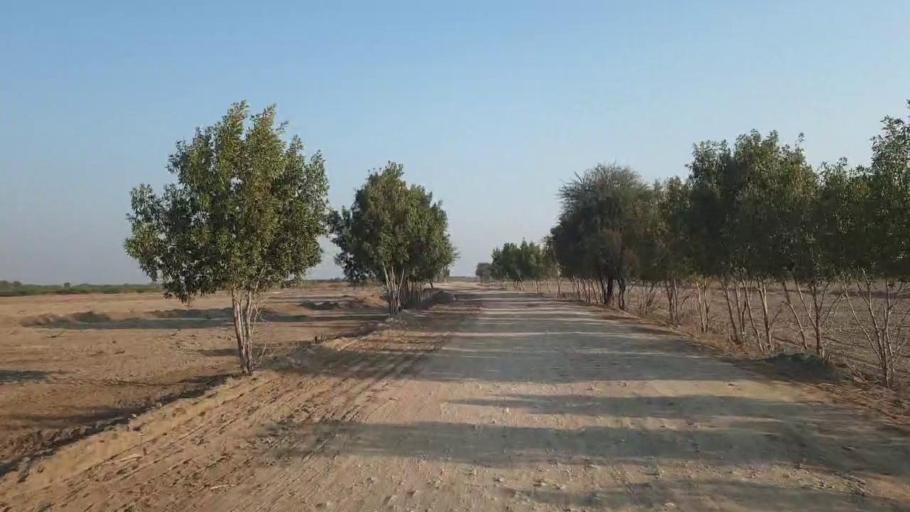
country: PK
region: Sindh
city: Mirpur Khas
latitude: 25.4282
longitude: 68.8997
